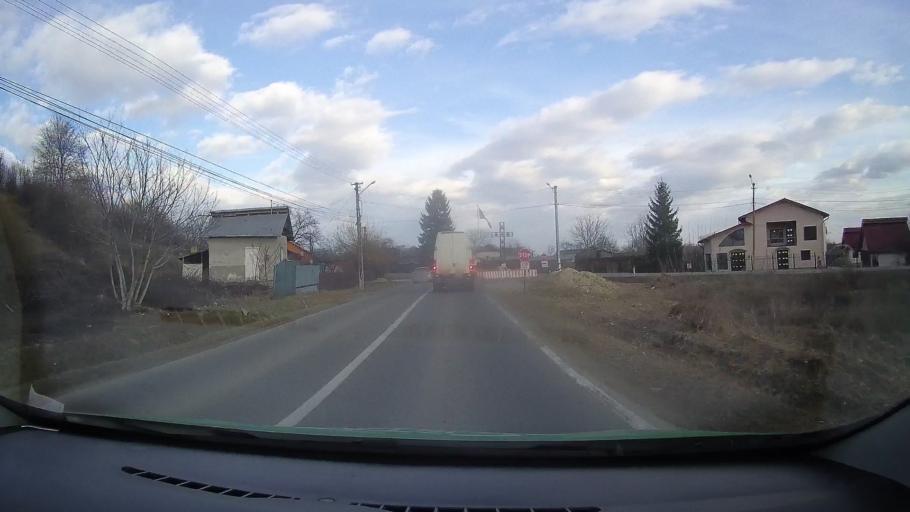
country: RO
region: Dambovita
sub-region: Comuna Gura Ocnitei
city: Gura Ocnitei
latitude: 44.9312
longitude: 25.5572
